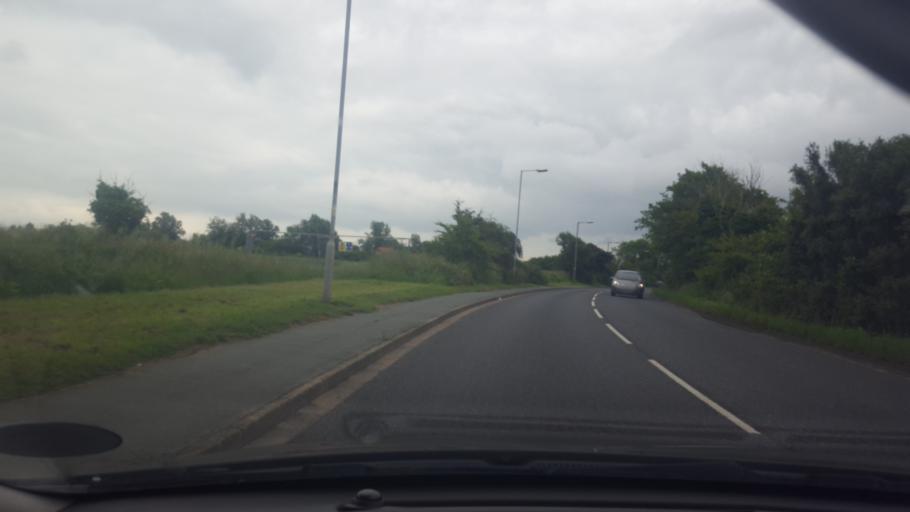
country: GB
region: England
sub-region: Essex
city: Clacton-on-Sea
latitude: 51.7827
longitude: 1.1232
